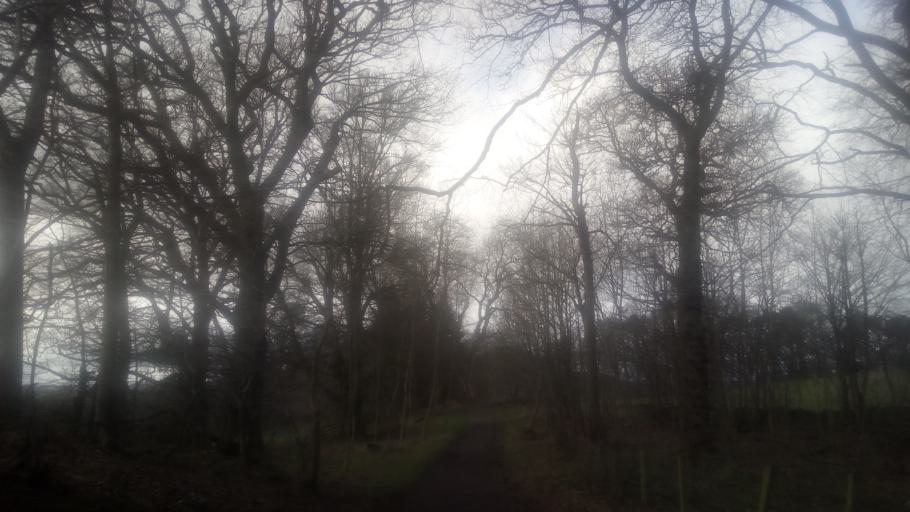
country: GB
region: Scotland
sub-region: The Scottish Borders
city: Saint Boswells
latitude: 55.5866
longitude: -2.6473
